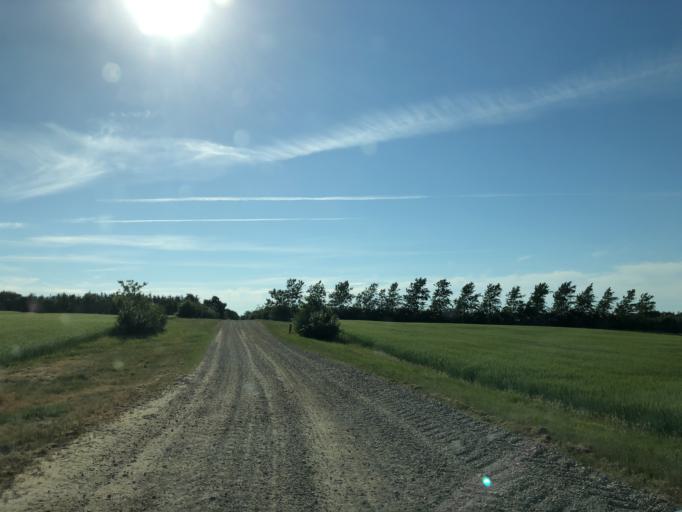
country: DK
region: Central Jutland
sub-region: Holstebro Kommune
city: Ulfborg
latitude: 56.3204
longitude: 8.3964
